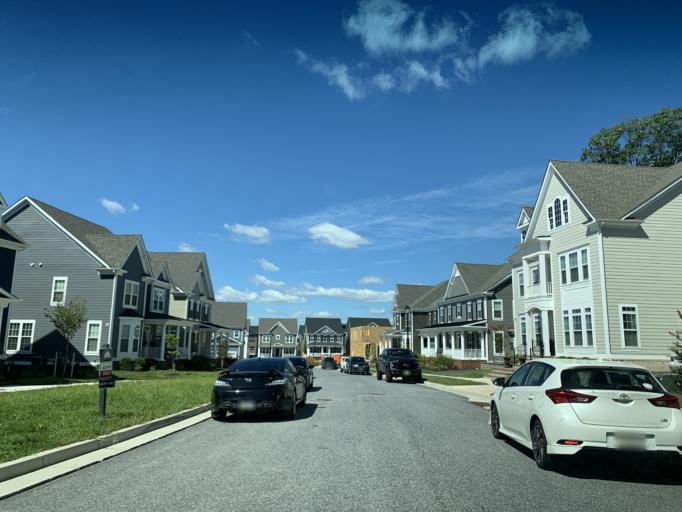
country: US
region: Maryland
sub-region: Baltimore County
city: Bowleys Quarters
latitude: 39.3615
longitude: -76.4004
